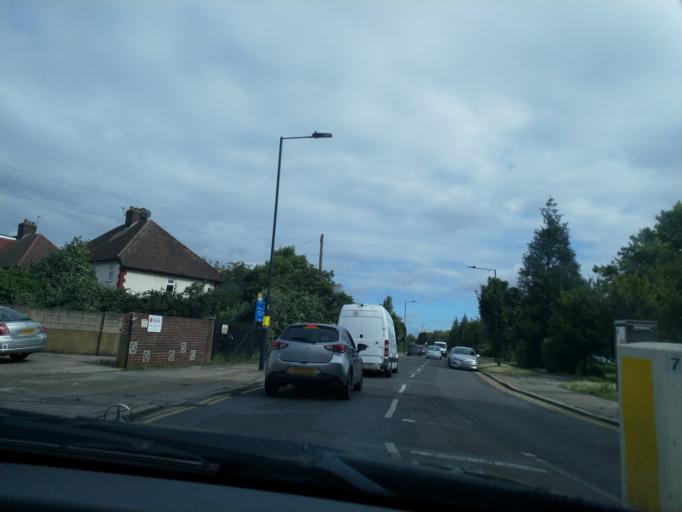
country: GB
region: England
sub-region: Greater London
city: Ealing Broadway
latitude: 51.5339
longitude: -0.3062
